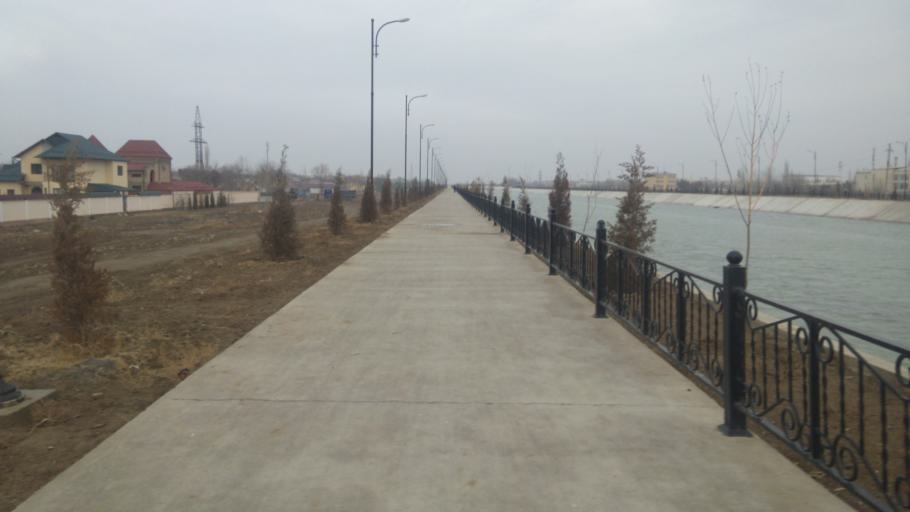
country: UZ
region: Sirdaryo
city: Guliston
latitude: 40.5052
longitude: 68.7811
